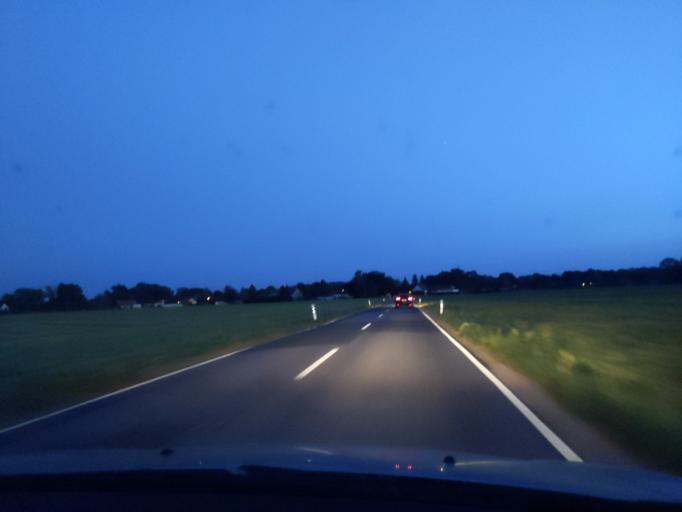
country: DE
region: Saxony
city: Malschwitz
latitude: 51.2704
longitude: 14.5222
